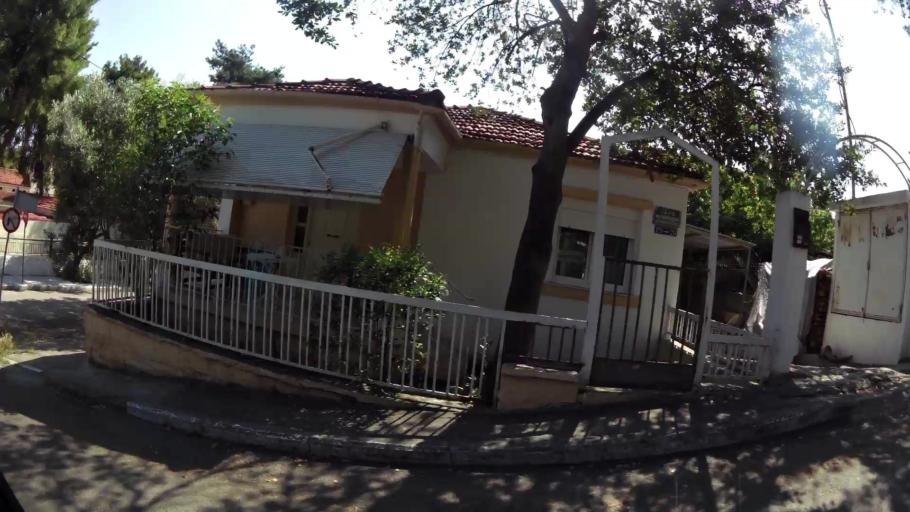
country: GR
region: Central Macedonia
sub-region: Nomos Thessalonikis
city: Peraia
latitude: 40.4977
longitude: 22.9263
